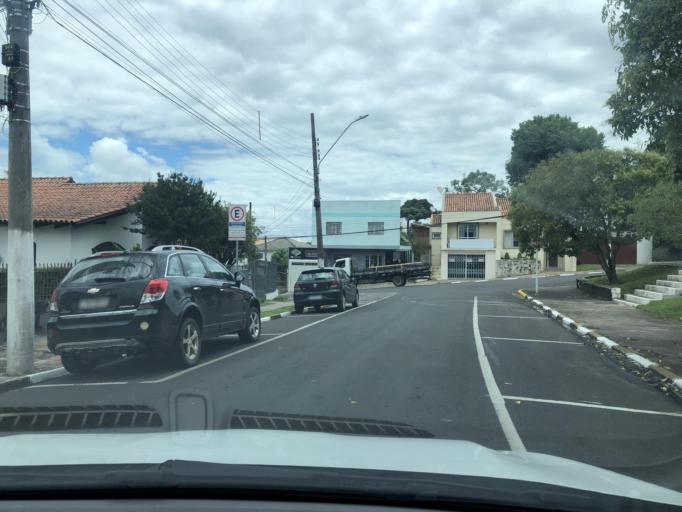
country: BR
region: Santa Catarina
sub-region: Lages
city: Lages
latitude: -27.8200
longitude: -50.3278
